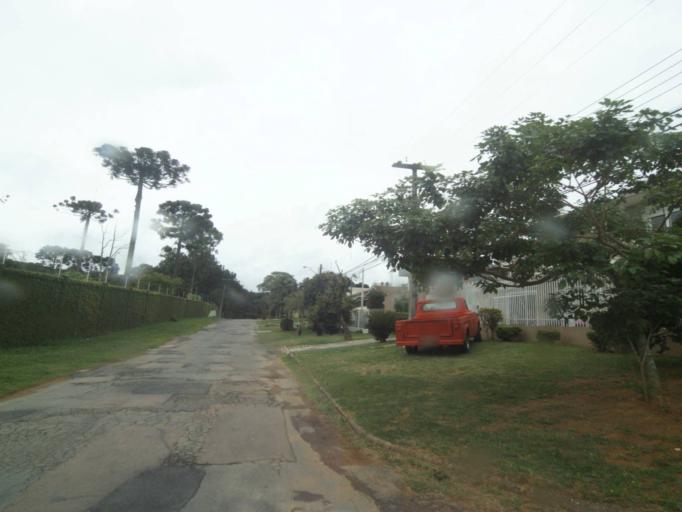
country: BR
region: Parana
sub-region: Curitiba
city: Curitiba
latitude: -25.4288
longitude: -49.3316
